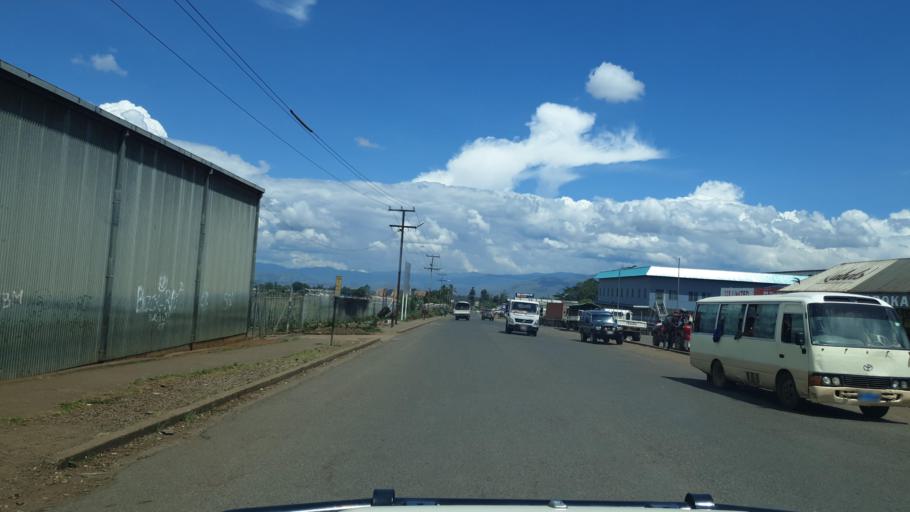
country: PG
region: Eastern Highlands
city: Goroka
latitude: -6.0819
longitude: 145.3897
